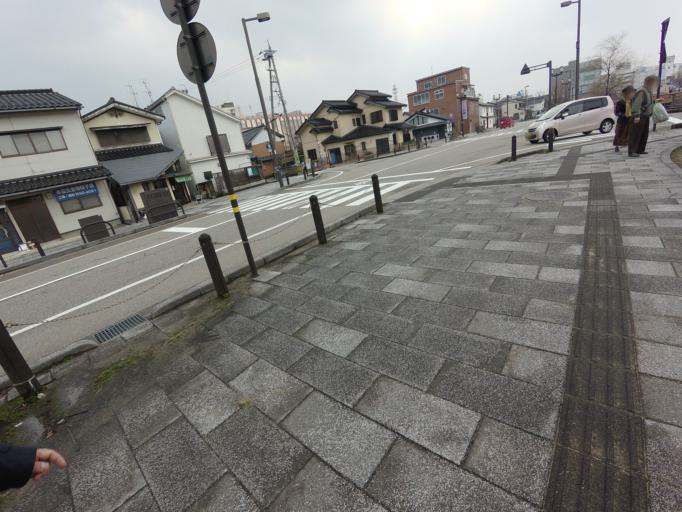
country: JP
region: Ishikawa
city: Nanao
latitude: 37.0469
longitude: 136.9666
